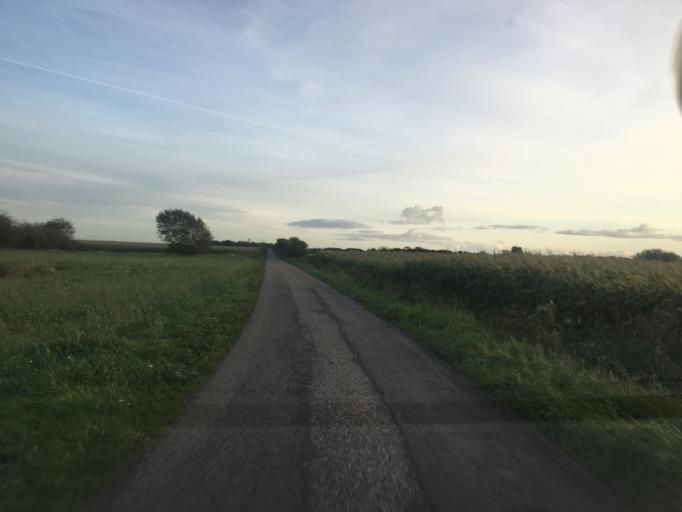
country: DK
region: South Denmark
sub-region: Tonder Kommune
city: Tonder
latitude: 54.9985
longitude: 8.9065
